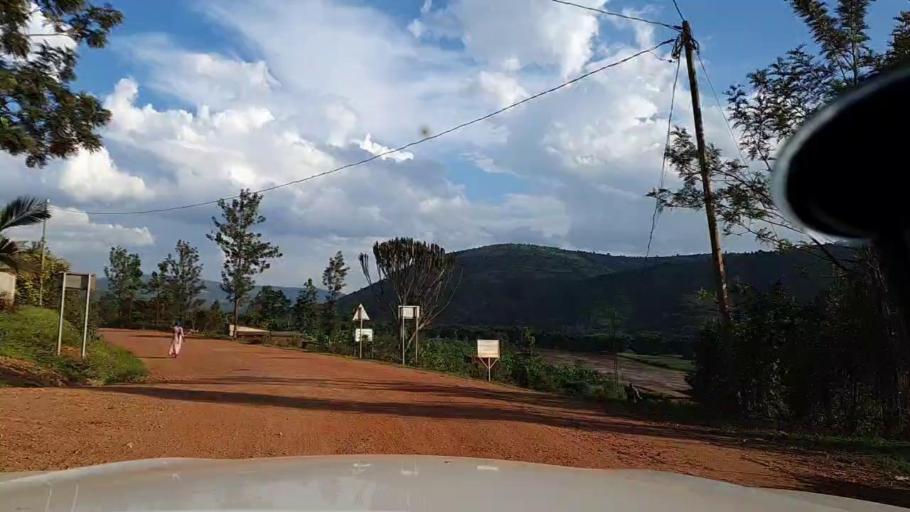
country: RW
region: Kigali
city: Kigali
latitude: -1.9024
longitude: 29.9642
